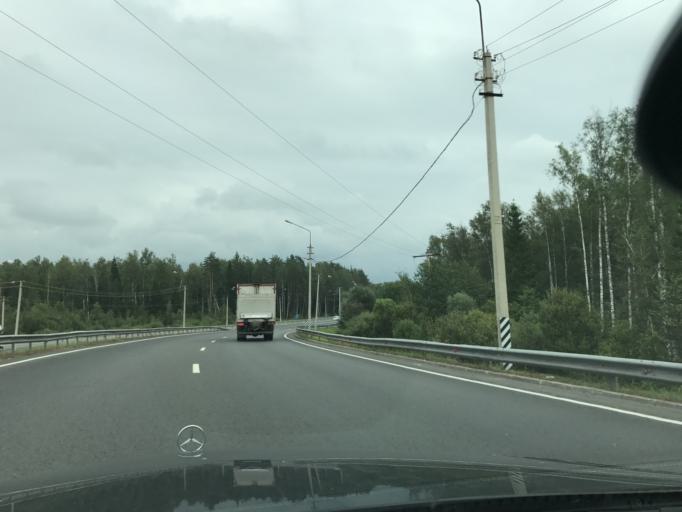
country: RU
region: Vladimir
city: Kameshkovo
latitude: 56.1934
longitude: 40.9522
